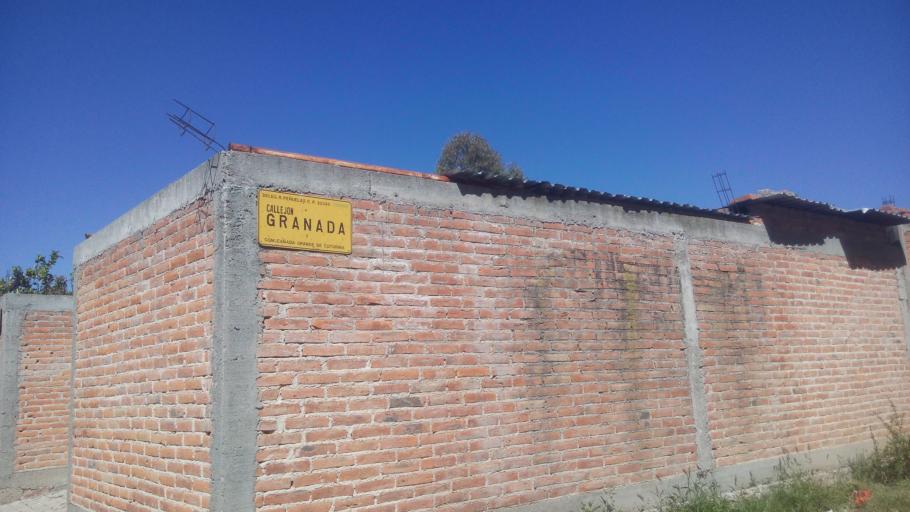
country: MX
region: Aguascalientes
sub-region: Aguascalientes
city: San Sebastian [Fraccionamiento]
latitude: 21.7827
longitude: -102.2364
